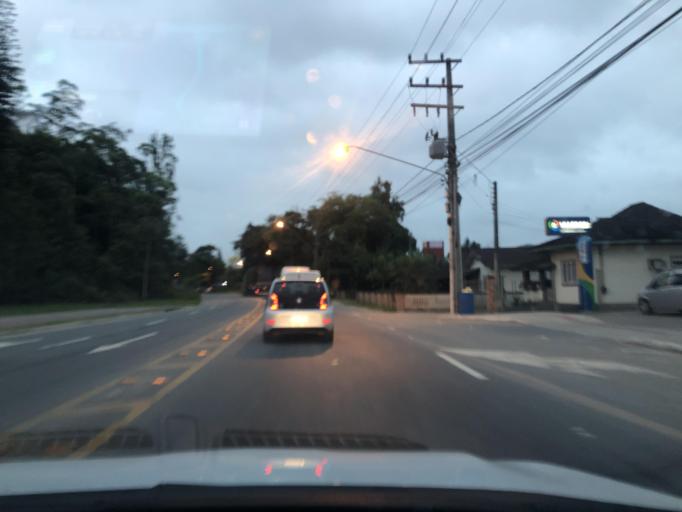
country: BR
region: Santa Catarina
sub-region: Pomerode
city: Pomerode
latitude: -26.7965
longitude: -49.0867
